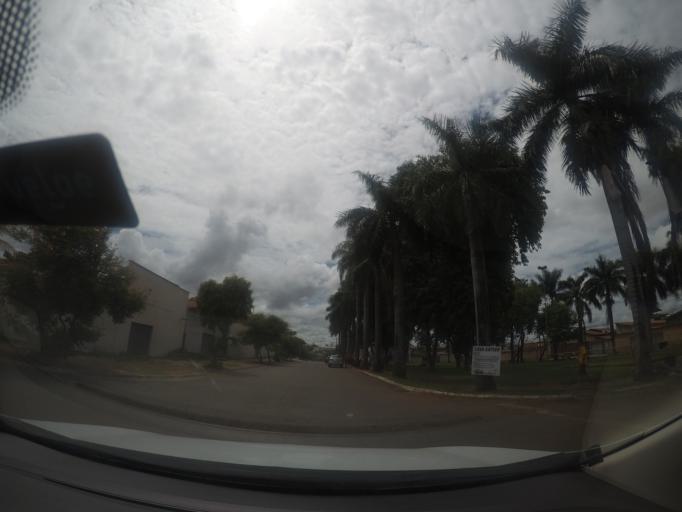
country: BR
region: Goias
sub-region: Goiania
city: Goiania
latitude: -16.6641
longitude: -49.3014
